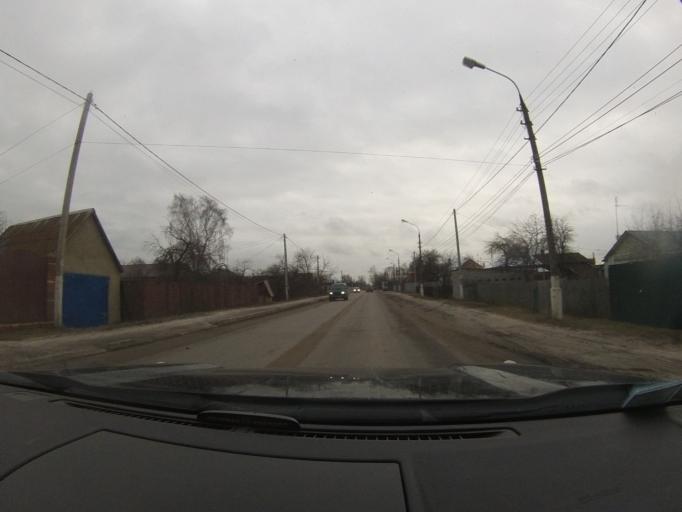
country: RU
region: Moskovskaya
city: Lopatinskiy
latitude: 55.3290
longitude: 38.7119
